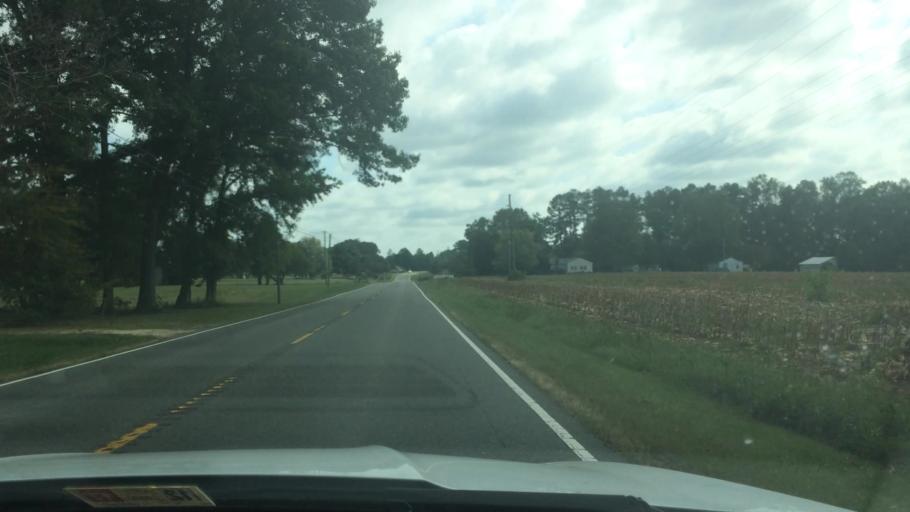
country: US
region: Virginia
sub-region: Northumberland County
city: Heathsville
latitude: 37.8430
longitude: -76.5795
